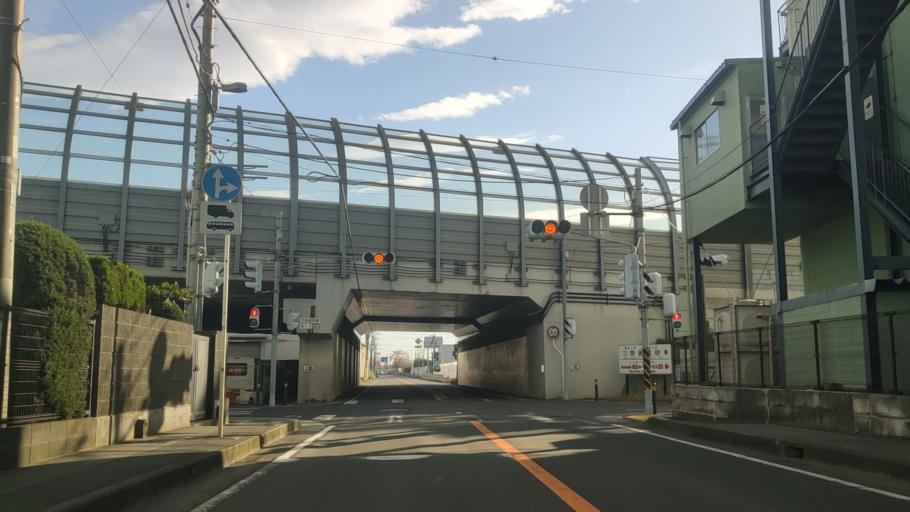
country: JP
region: Kanagawa
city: Atsugi
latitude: 35.4248
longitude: 139.3874
